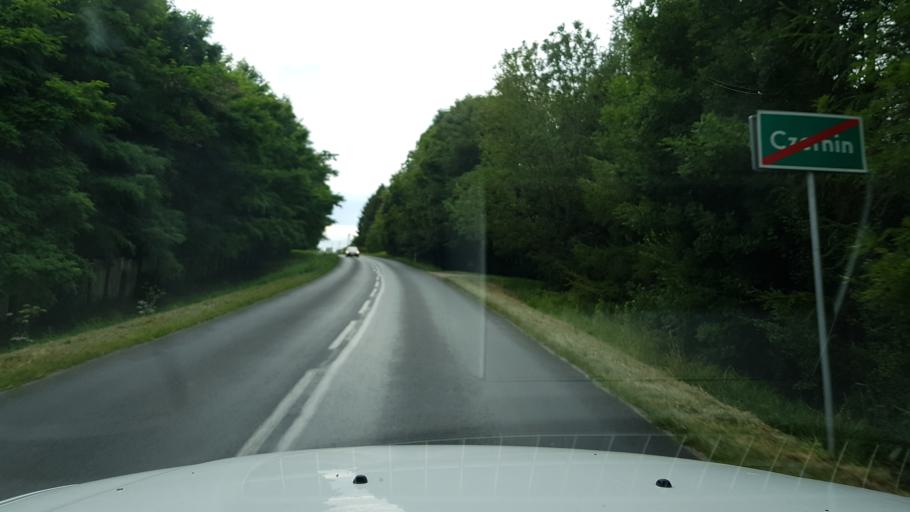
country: PL
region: West Pomeranian Voivodeship
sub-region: Powiat kolobrzeski
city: Dygowo
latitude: 54.1400
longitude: 15.7019
